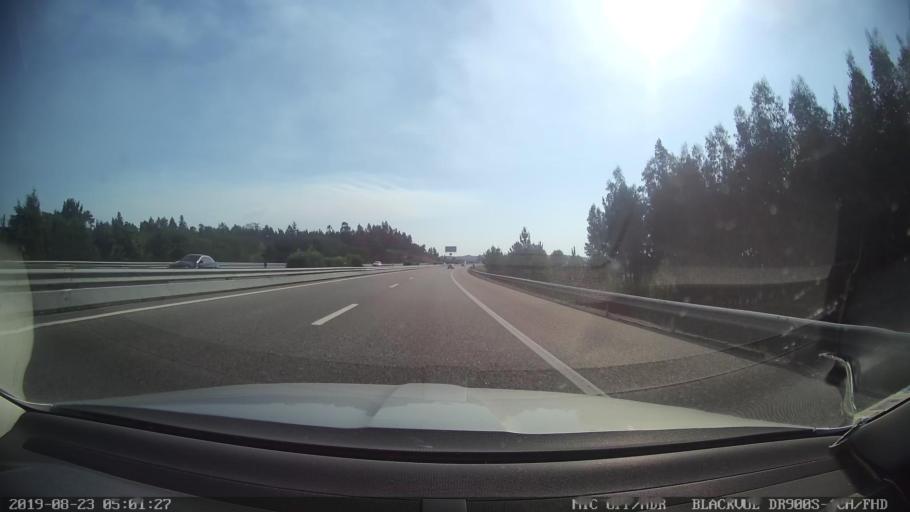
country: PT
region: Leiria
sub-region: Pombal
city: Pombal
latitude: 39.9806
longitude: -8.6274
